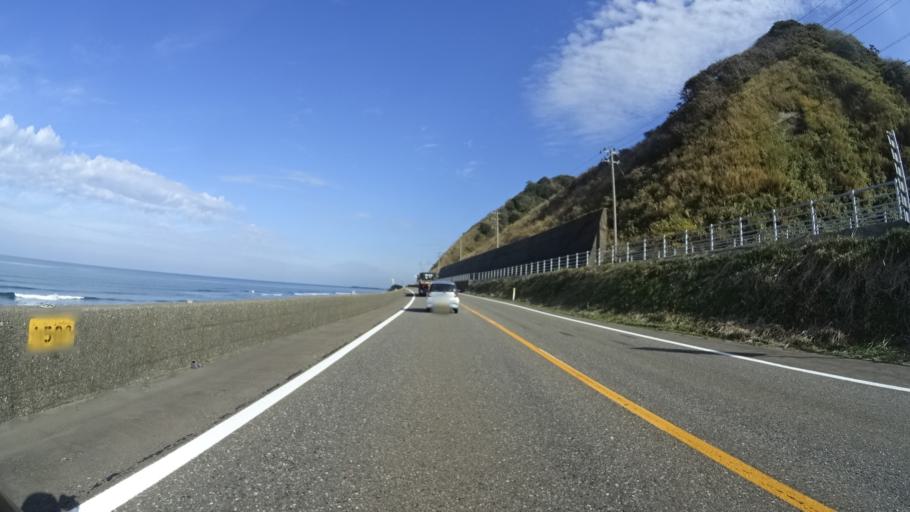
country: JP
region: Niigata
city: Joetsu
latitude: 37.1465
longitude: 138.0663
